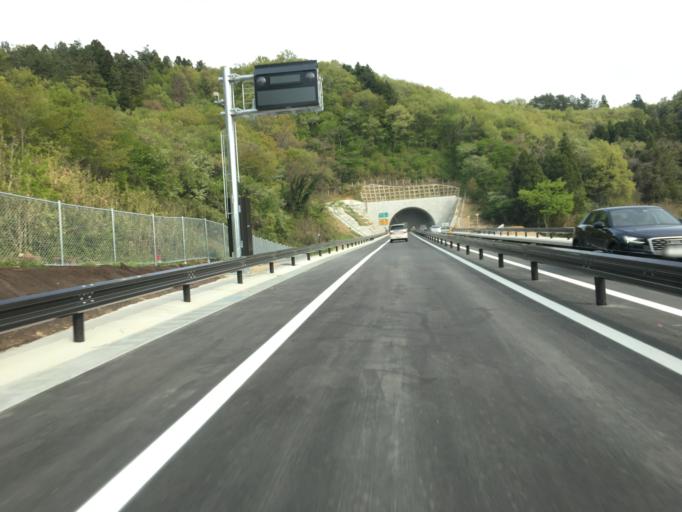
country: JP
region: Fukushima
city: Hobaramachi
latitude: 37.7874
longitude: 140.5627
